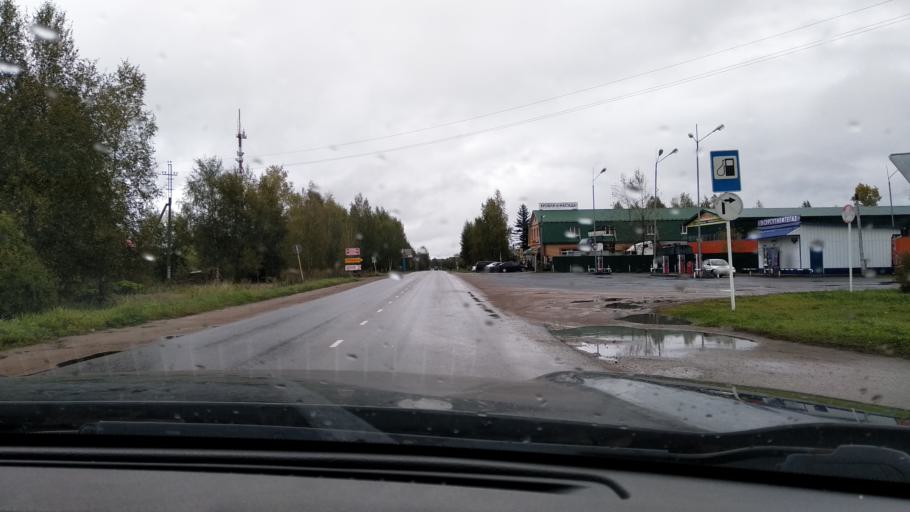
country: RU
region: Tverskaya
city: Kashin
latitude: 57.3582
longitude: 37.5804
